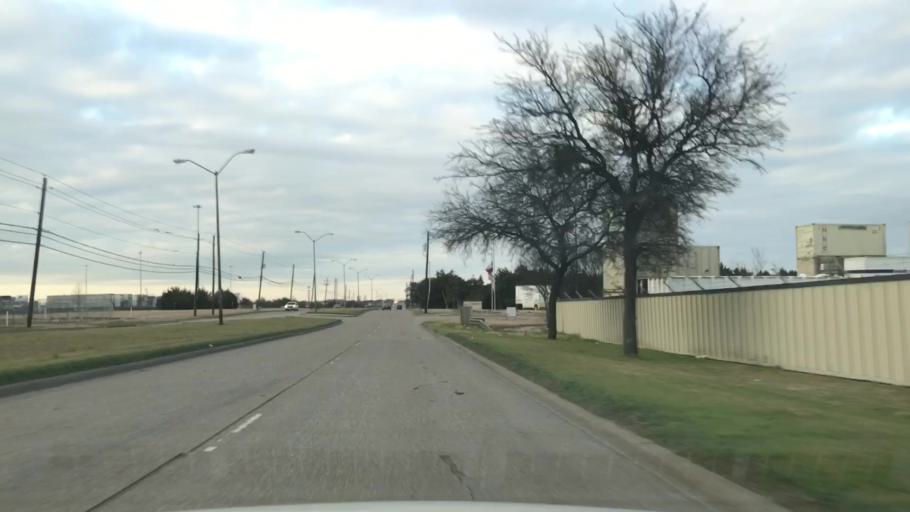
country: US
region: Texas
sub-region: Dallas County
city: Cockrell Hill
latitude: 32.6999
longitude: -96.9086
